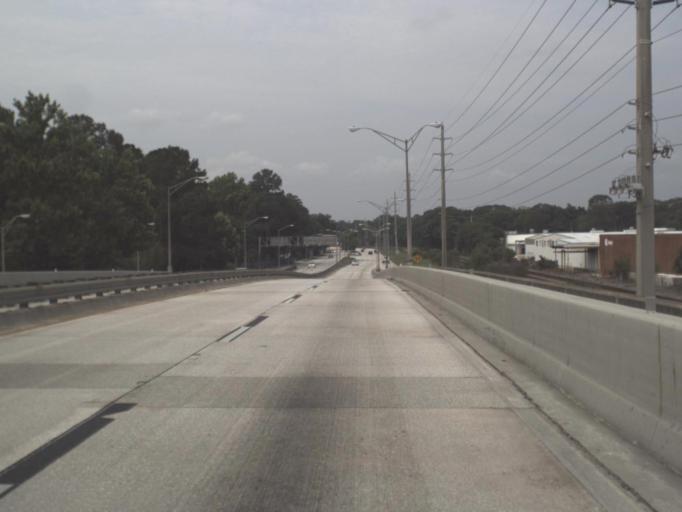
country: US
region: Florida
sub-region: Duval County
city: Jacksonville
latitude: 30.3076
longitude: -81.7132
